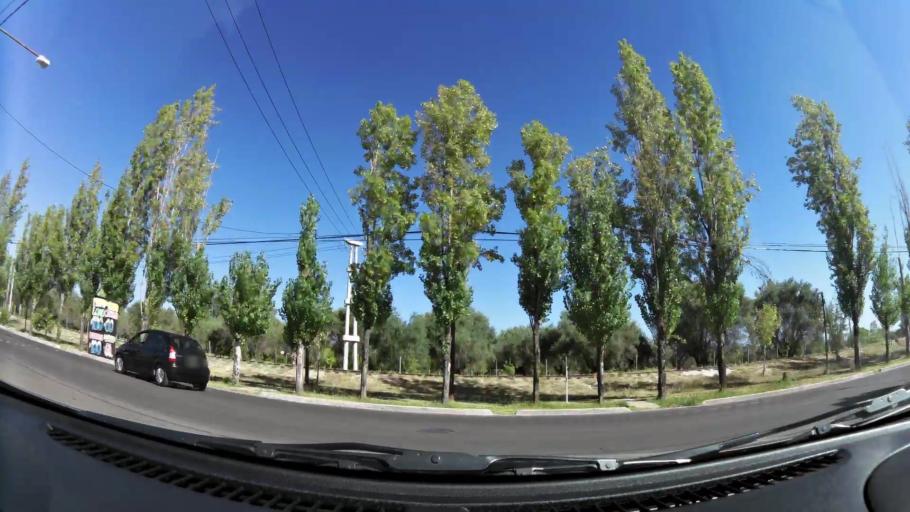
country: AR
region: Mendoza
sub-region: Departamento de Maipu
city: Maipu
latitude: -32.9730
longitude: -68.8002
